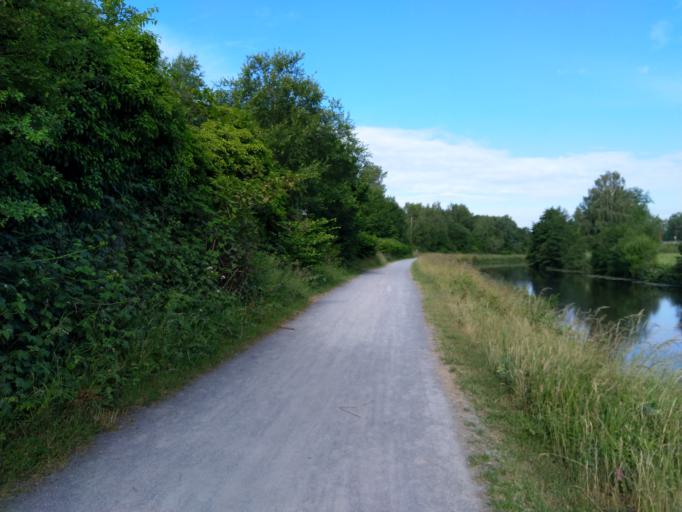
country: FR
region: Nord-Pas-de-Calais
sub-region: Departement du Nord
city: Jeumont
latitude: 50.2984
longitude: 4.0938
